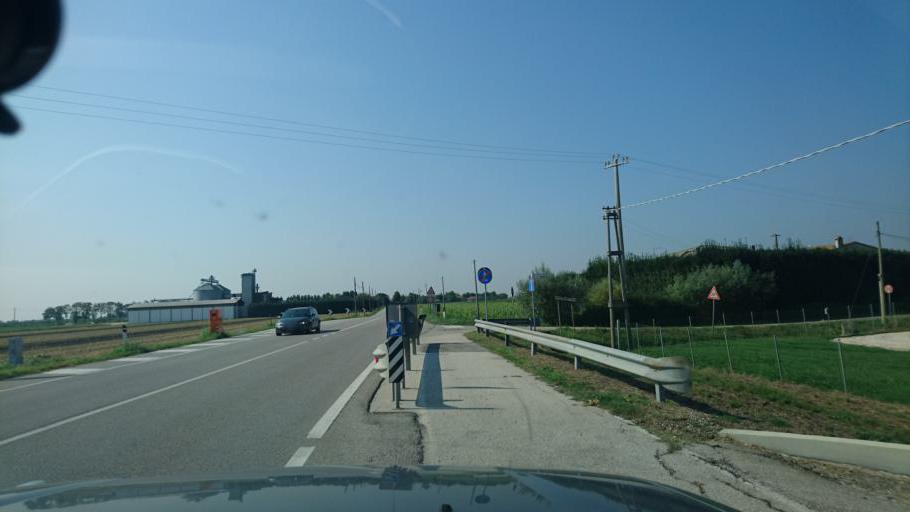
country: IT
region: Veneto
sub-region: Provincia di Padova
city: Bovolenta
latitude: 45.2632
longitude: 11.9282
